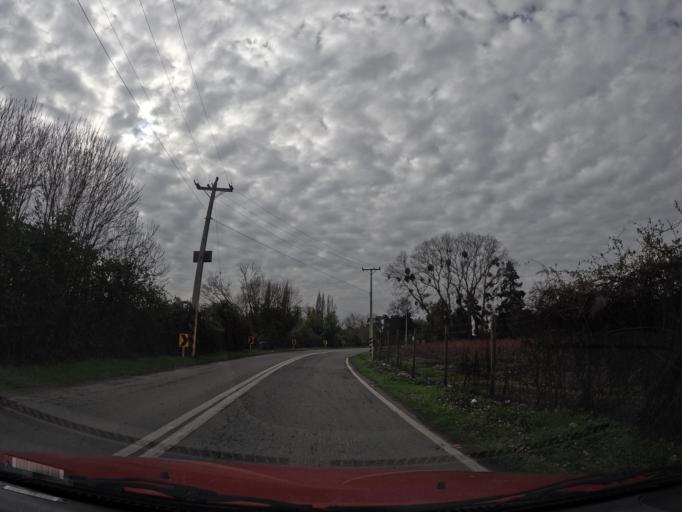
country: CL
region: Maule
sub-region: Provincia de Linares
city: Linares
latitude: -35.8560
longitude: -71.6149
